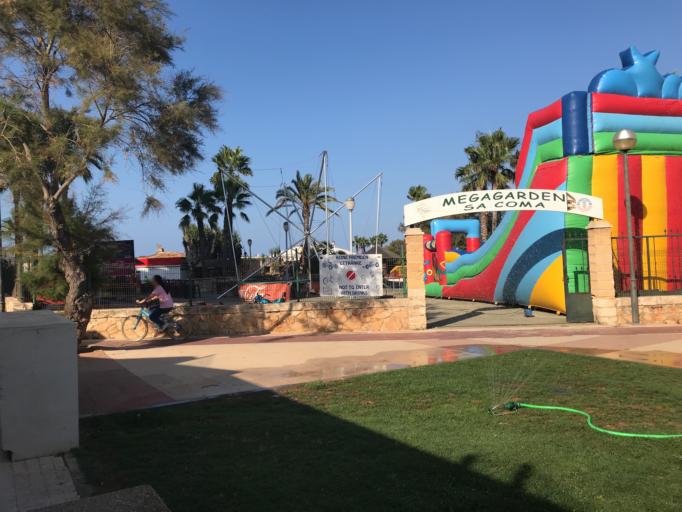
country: ES
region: Balearic Islands
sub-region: Illes Balears
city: Son Servera
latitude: 39.5698
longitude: 3.3748
